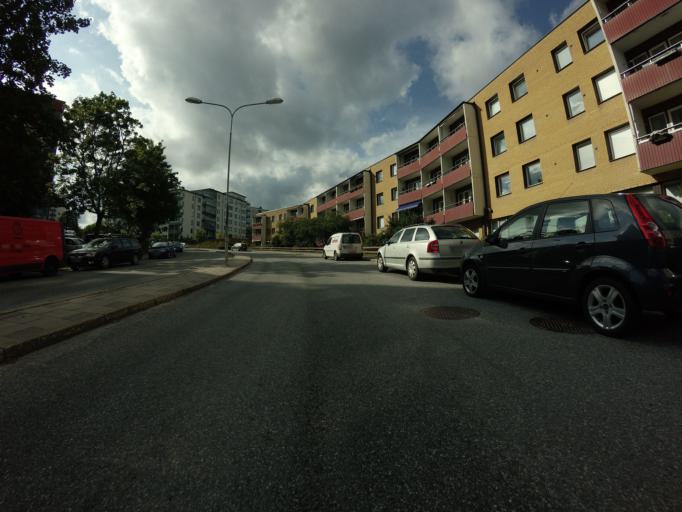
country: SE
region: Stockholm
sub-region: Lidingo
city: Lidingoe
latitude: 59.3734
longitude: 18.1470
